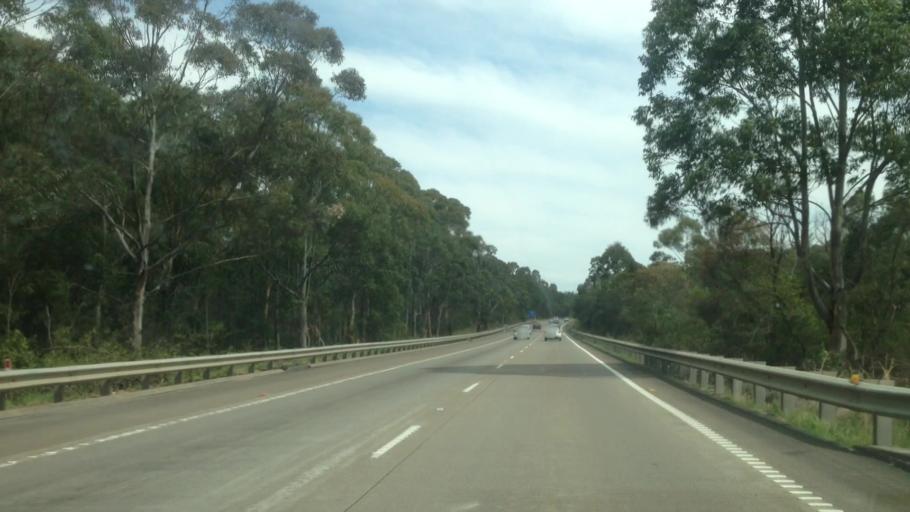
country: AU
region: New South Wales
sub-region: Lake Macquarie Shire
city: Fennell Bay
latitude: -32.9711
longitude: 151.5340
